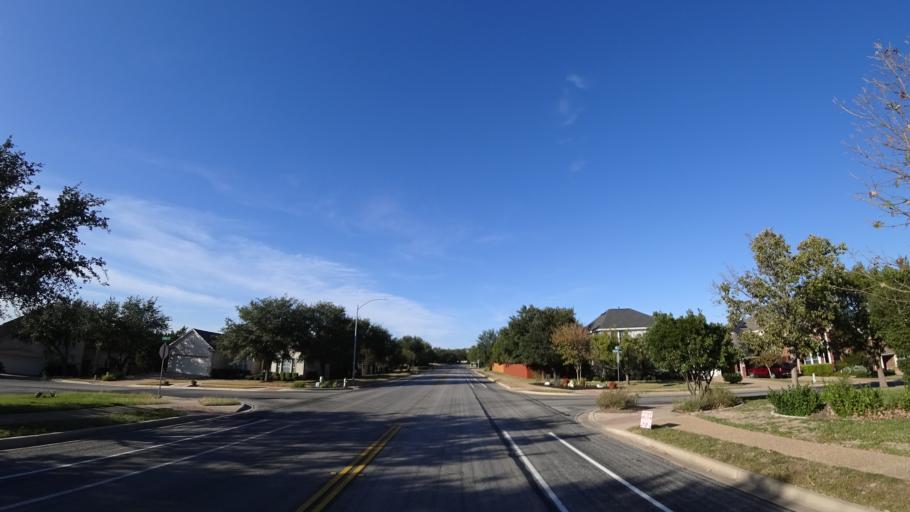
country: US
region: Texas
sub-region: Williamson County
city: Jollyville
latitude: 30.4064
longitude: -97.7764
